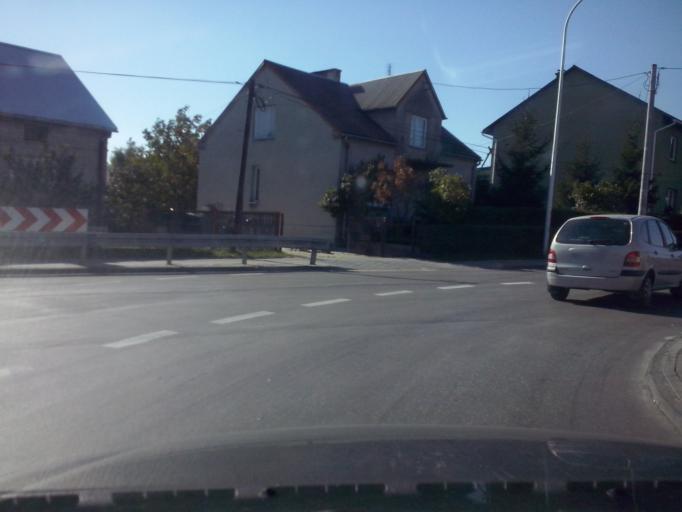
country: PL
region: Lublin Voivodeship
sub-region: Powiat bilgorajski
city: Bilgoraj
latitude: 50.5251
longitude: 22.7153
